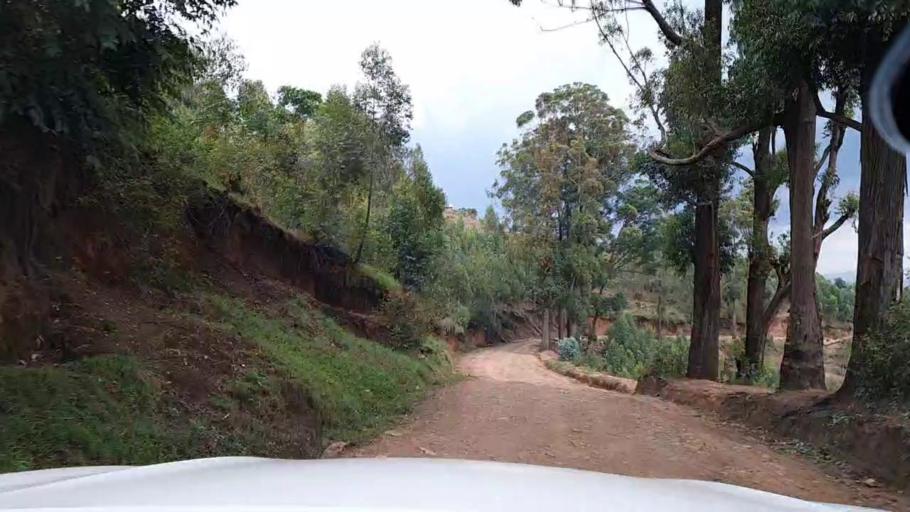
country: BI
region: Kayanza
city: Kayanza
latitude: -2.7940
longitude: 29.5167
